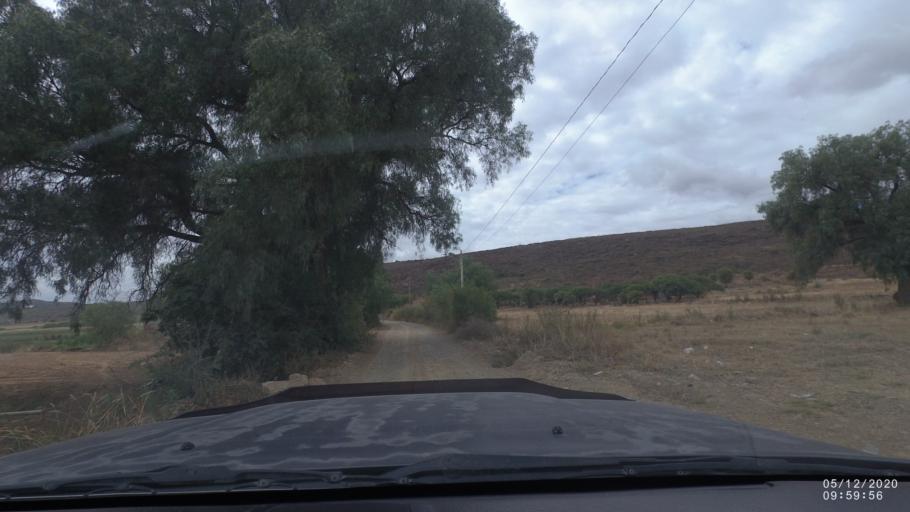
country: BO
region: Cochabamba
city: Sipe Sipe
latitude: -17.4350
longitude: -66.2912
